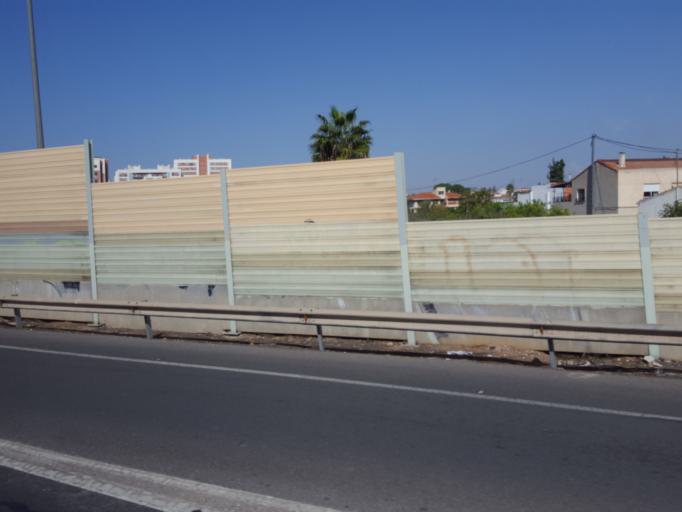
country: ES
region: Murcia
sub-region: Murcia
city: Murcia
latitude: 38.0002
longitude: -1.1550
